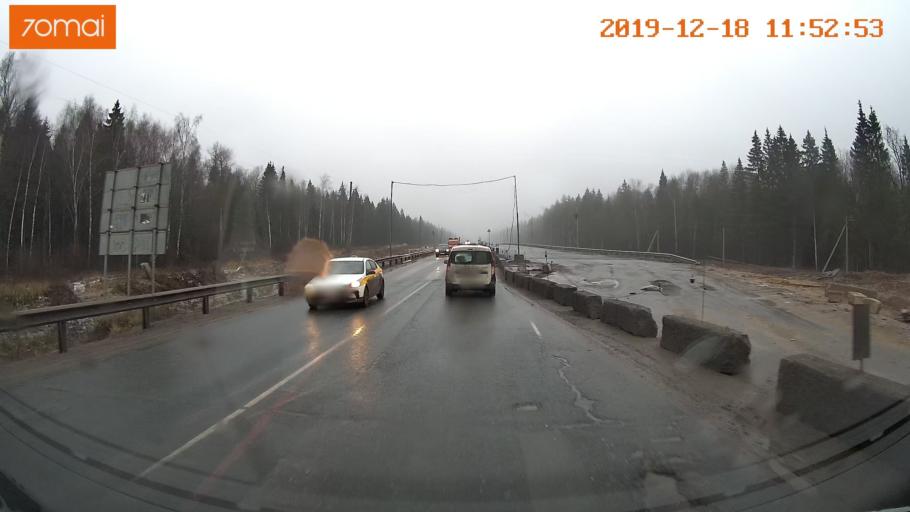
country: RU
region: Moskovskaya
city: Yershovo
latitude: 55.7988
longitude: 36.9209
